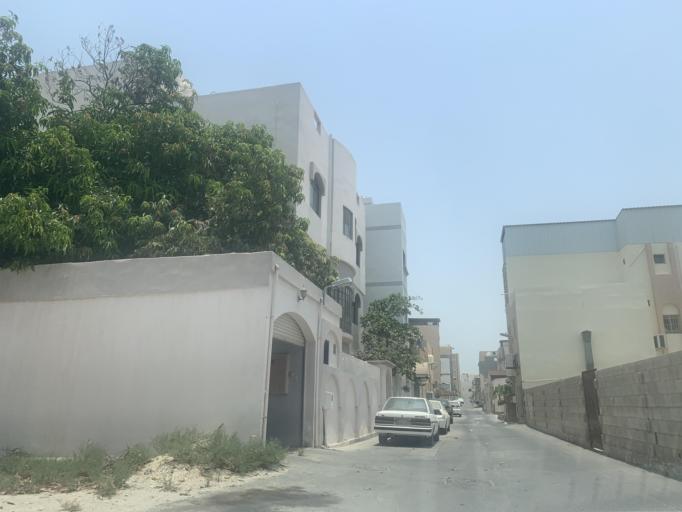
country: BH
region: Manama
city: Jidd Hafs
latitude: 26.2192
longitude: 50.4585
